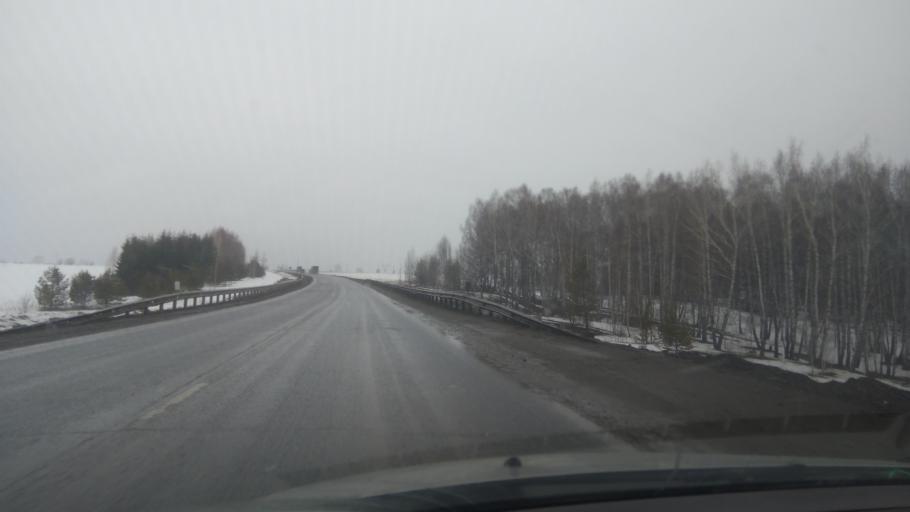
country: RU
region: Perm
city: Kungur
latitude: 57.3911
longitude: 56.9029
